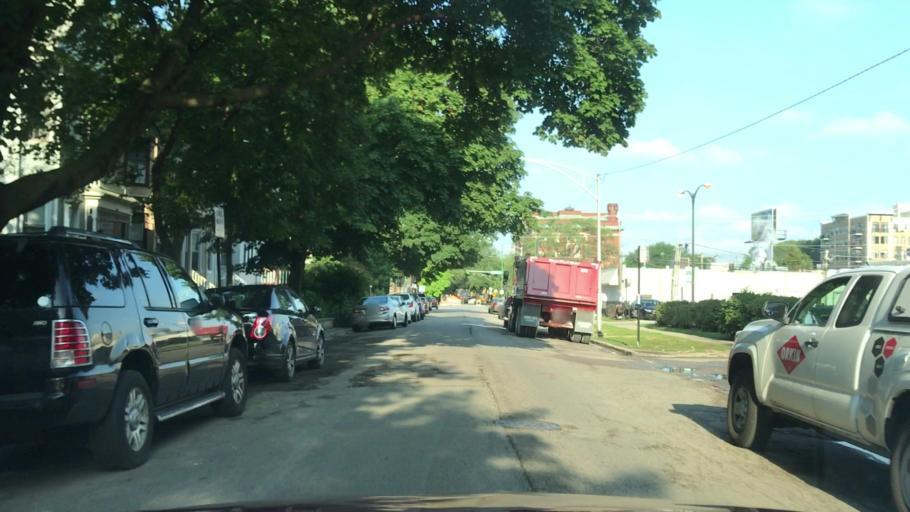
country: US
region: Illinois
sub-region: Cook County
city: Chicago
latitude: 41.9379
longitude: -87.6670
